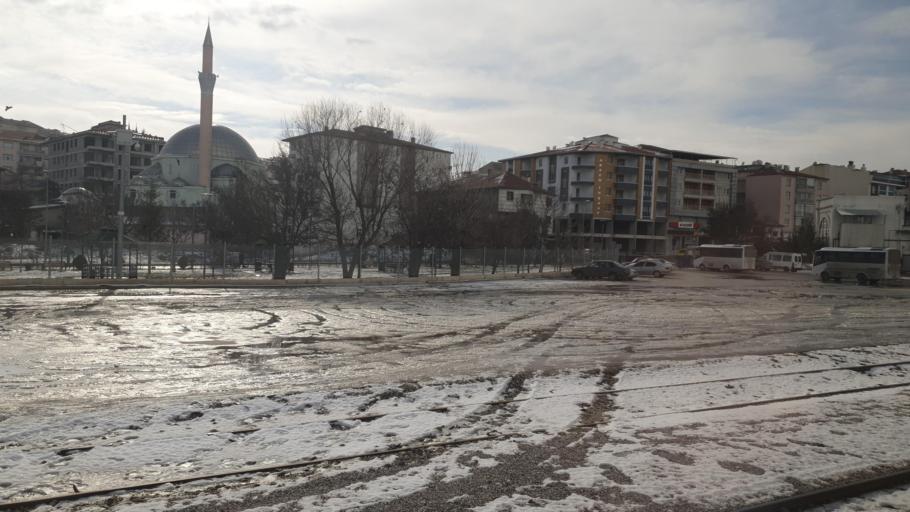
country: TR
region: Ankara
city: Elmadag
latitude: 39.9241
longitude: 33.2278
